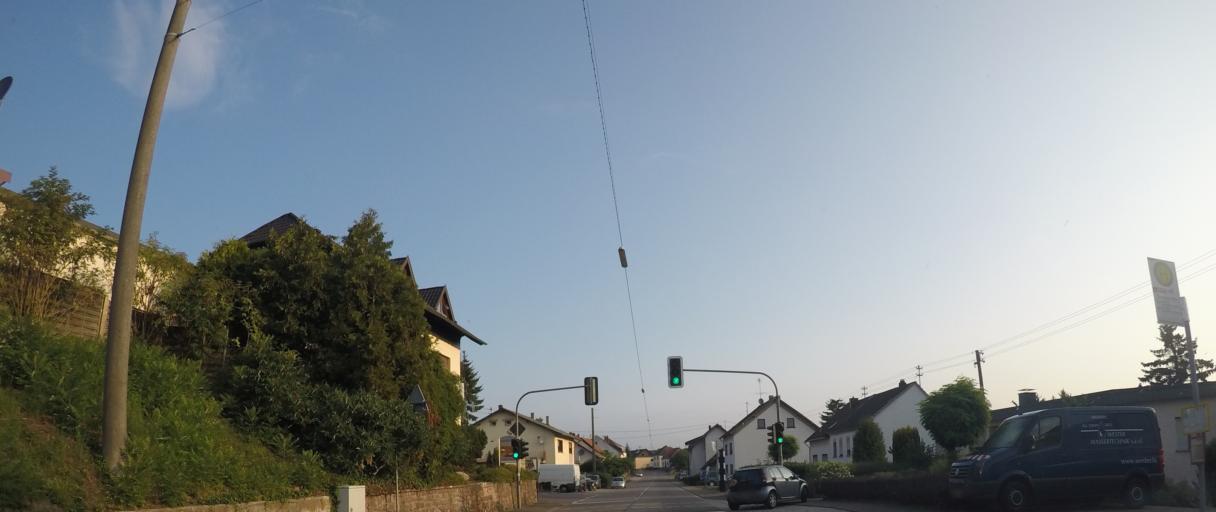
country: DE
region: Saarland
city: Lebach
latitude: 49.3857
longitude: 6.9273
